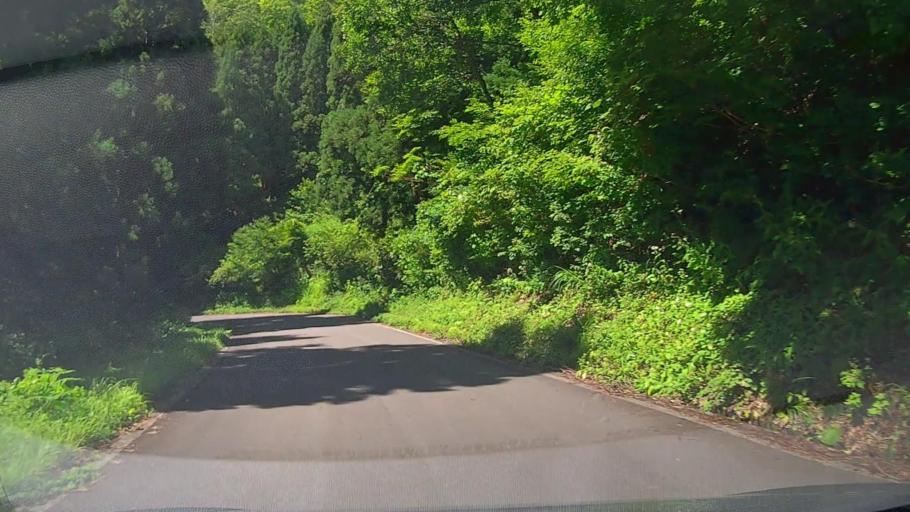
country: JP
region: Nagano
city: Iiyama
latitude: 36.9308
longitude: 138.4492
